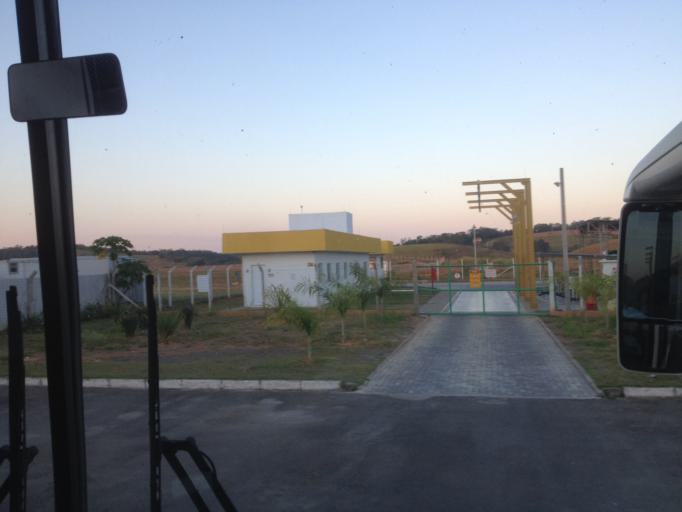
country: BR
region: Minas Gerais
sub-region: Rio Novo
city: Rio Novo
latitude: -21.5102
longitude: -43.1615
